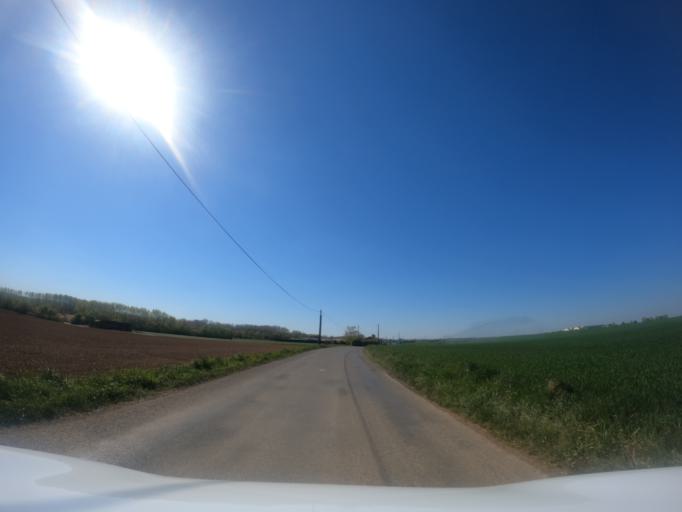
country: FR
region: Pays de la Loire
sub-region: Departement de la Vendee
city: Fontenay-le-Comte
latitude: 46.4129
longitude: -0.7882
